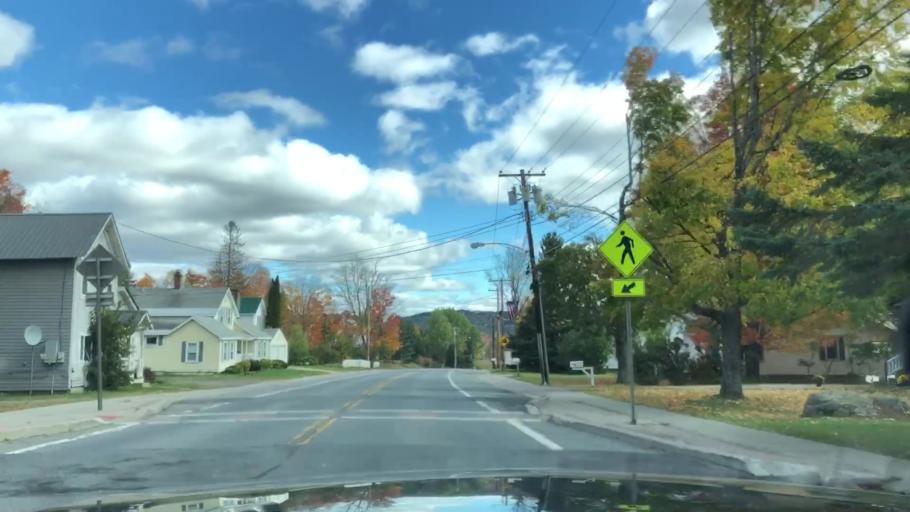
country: US
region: New York
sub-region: Hamilton County
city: Lake Pleasant
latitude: 43.7823
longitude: -74.2623
